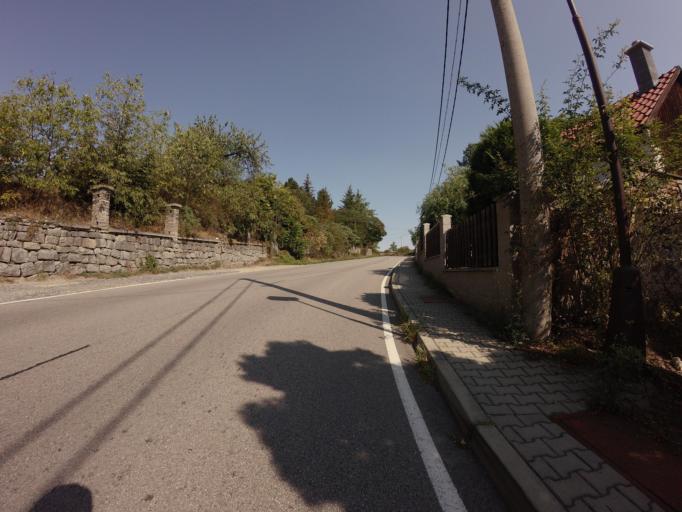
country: CZ
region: Central Bohemia
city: Kamenny Privoz
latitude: 49.8580
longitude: 14.5161
